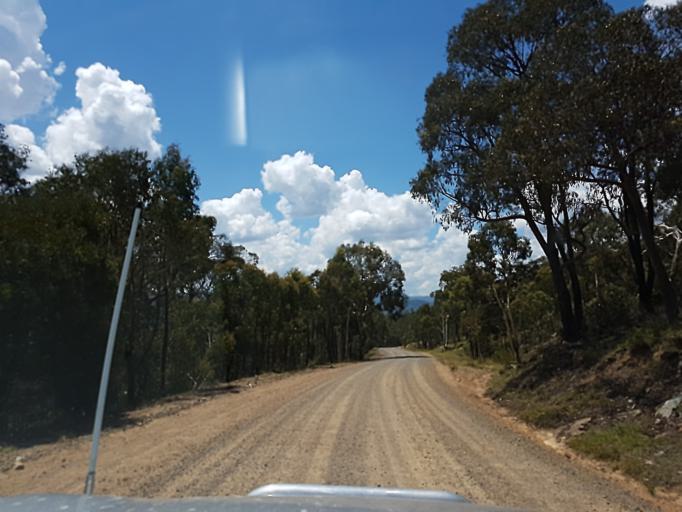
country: AU
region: Victoria
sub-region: Alpine
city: Mount Beauty
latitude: -36.8997
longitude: 147.8169
